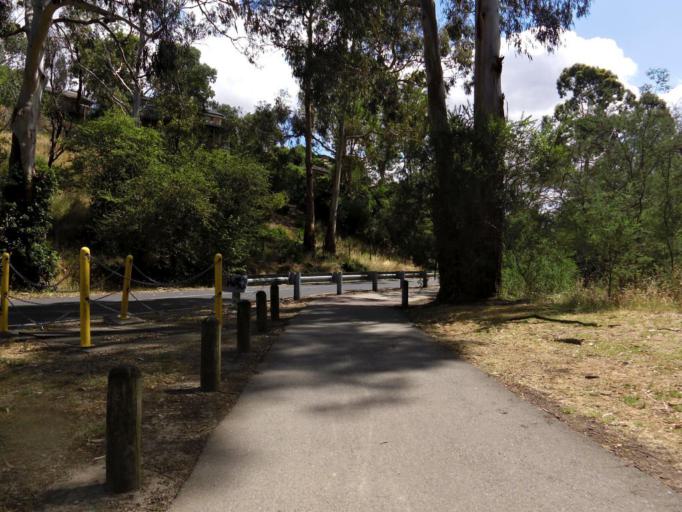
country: AU
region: Victoria
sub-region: Nillumbik
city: Diamond Creek
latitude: -37.6770
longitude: 145.1500
